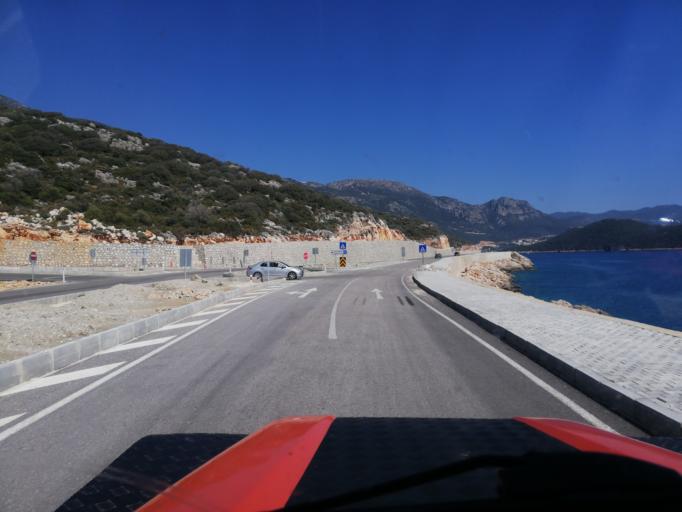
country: TR
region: Antalya
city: Kas
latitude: 36.2019
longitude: 29.5868
